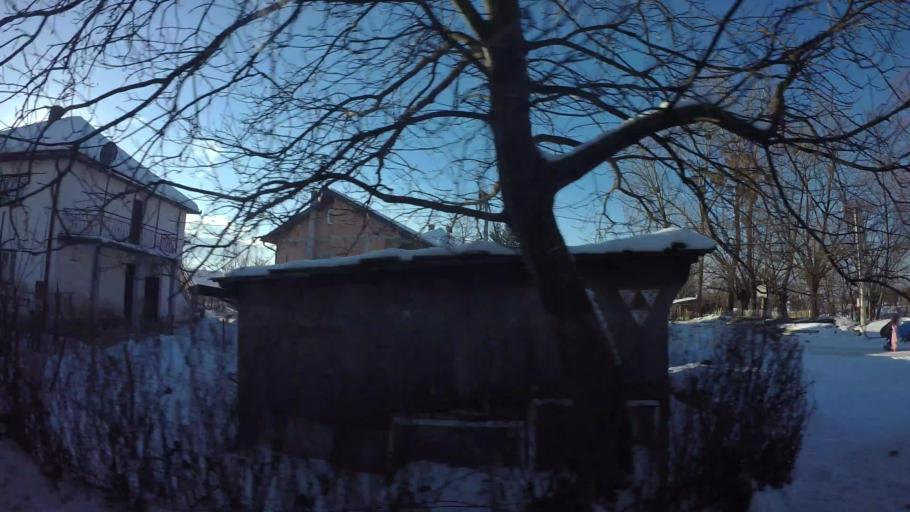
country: BA
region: Federation of Bosnia and Herzegovina
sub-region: Kanton Sarajevo
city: Sarajevo
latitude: 43.8157
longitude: 18.3466
